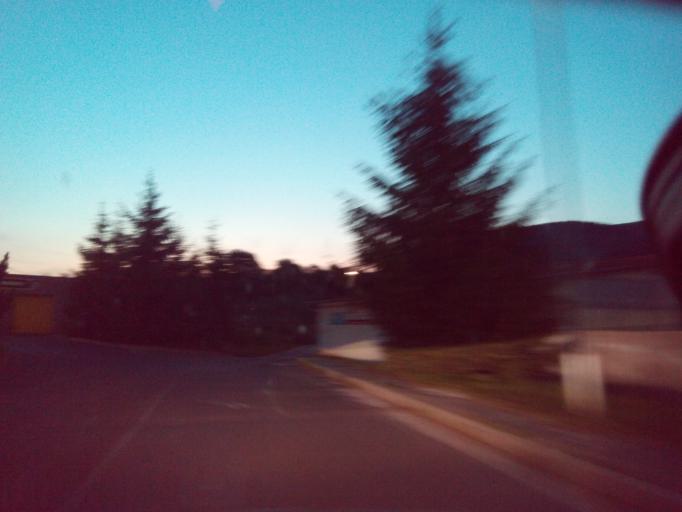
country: SK
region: Kosicky
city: Krompachy
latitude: 48.9170
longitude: 20.8715
